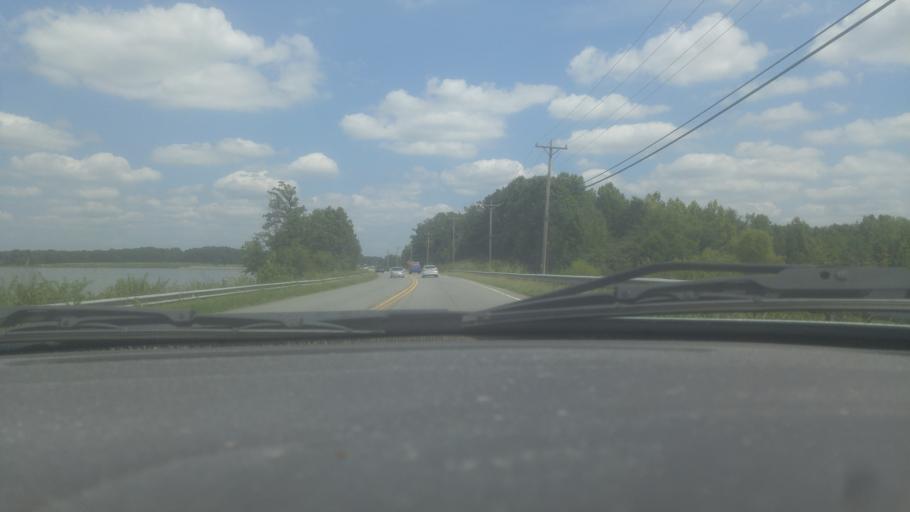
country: US
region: North Carolina
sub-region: Cabarrus County
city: Kannapolis
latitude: 35.4373
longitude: -80.7083
